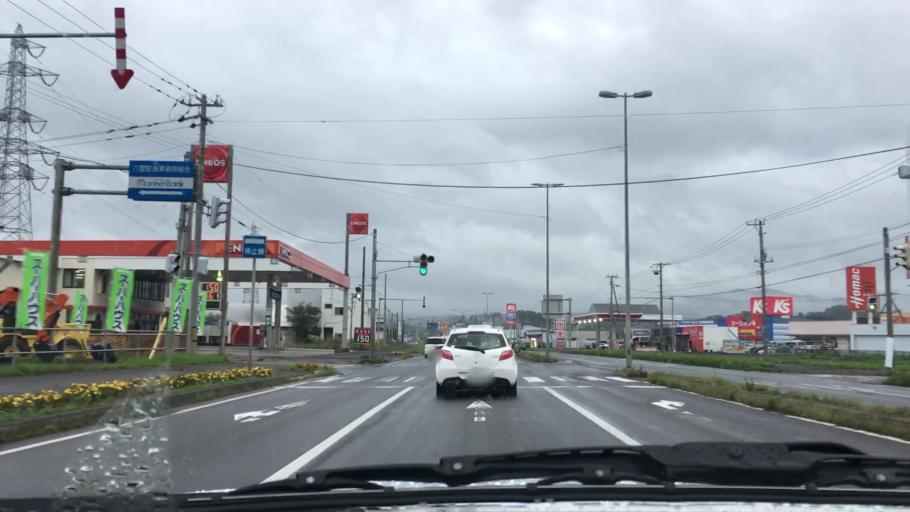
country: JP
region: Hokkaido
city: Nanae
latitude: 42.2517
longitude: 140.2848
